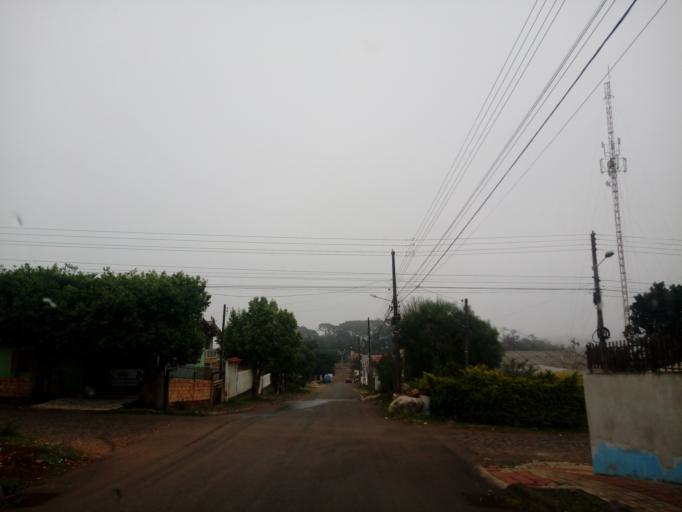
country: BR
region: Santa Catarina
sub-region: Chapeco
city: Chapeco
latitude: -27.1063
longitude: -52.6756
